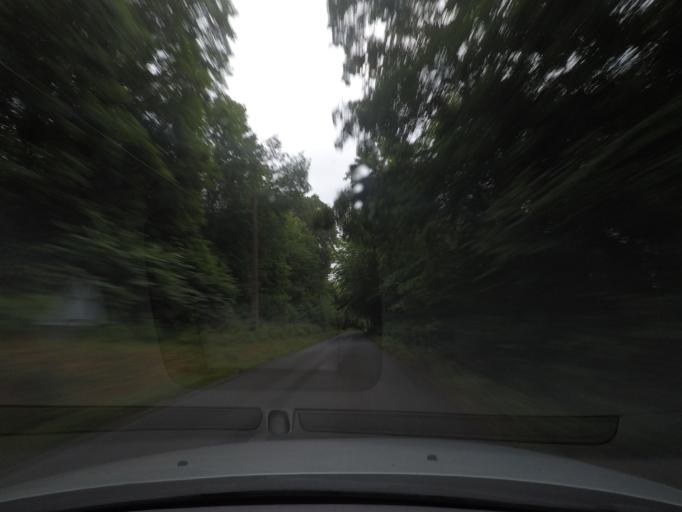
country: FR
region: Haute-Normandie
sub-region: Departement de la Seine-Maritime
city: Fontaine-le-Bourg
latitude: 49.5682
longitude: 1.1725
